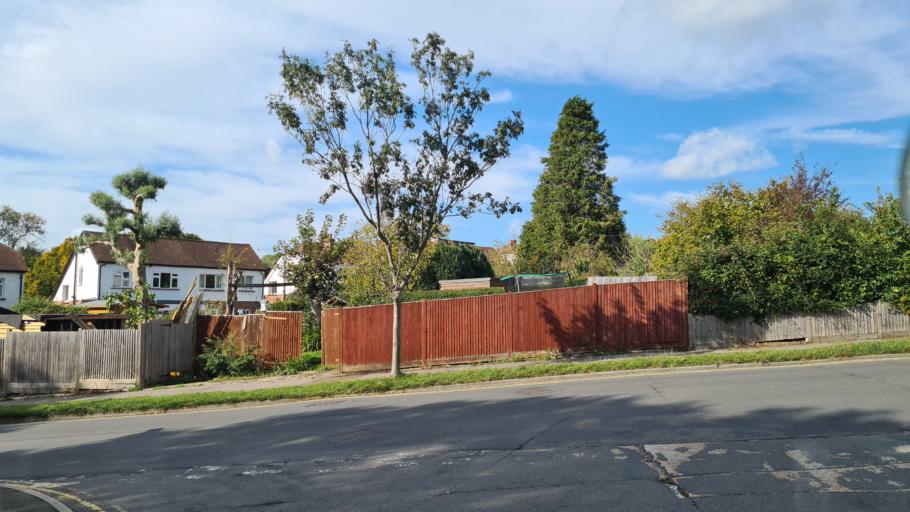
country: GB
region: England
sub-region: East Sussex
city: Hastings
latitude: 50.8739
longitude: 0.5660
